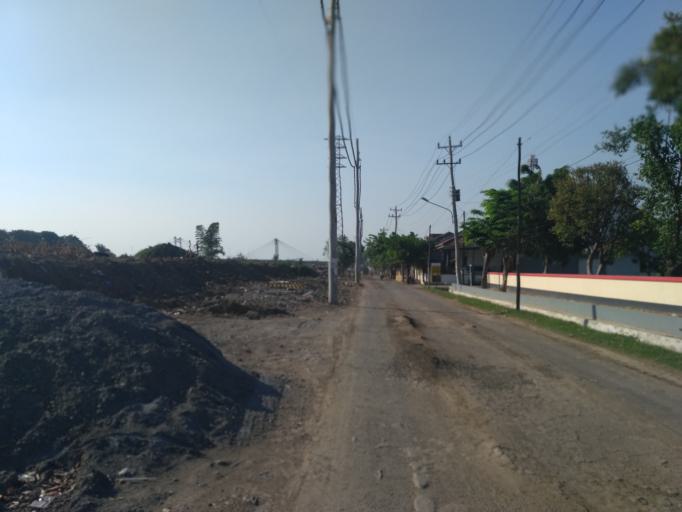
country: ID
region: Central Java
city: Semarang
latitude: -6.9895
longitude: 110.4411
